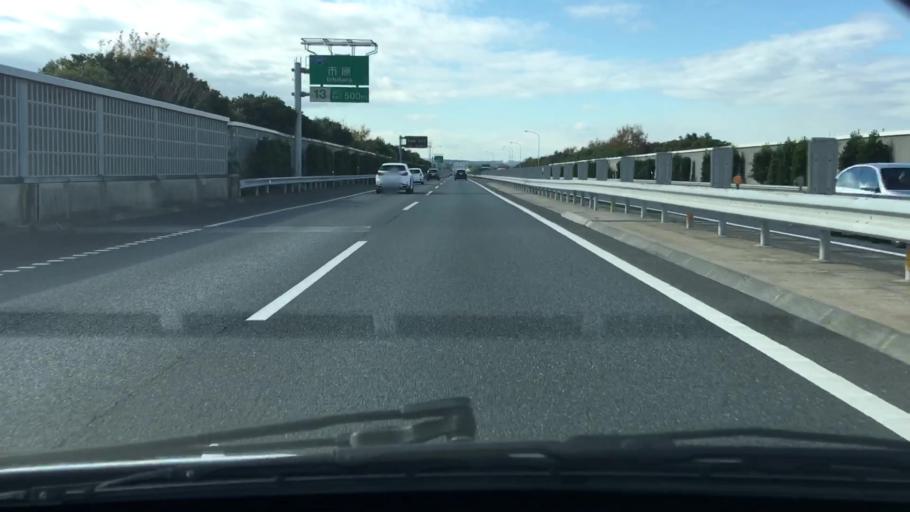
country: JP
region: Chiba
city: Ichihara
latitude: 35.4997
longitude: 140.0975
